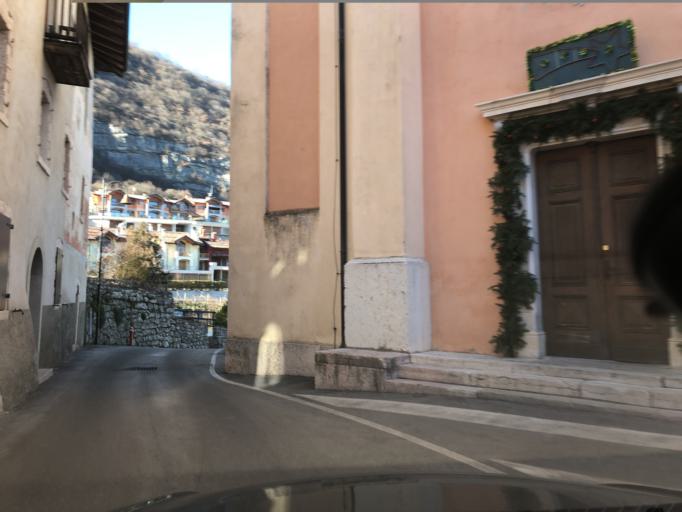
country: IT
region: Trentino-Alto Adige
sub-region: Provincia di Trento
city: Mori
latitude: 45.8384
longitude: 10.9706
